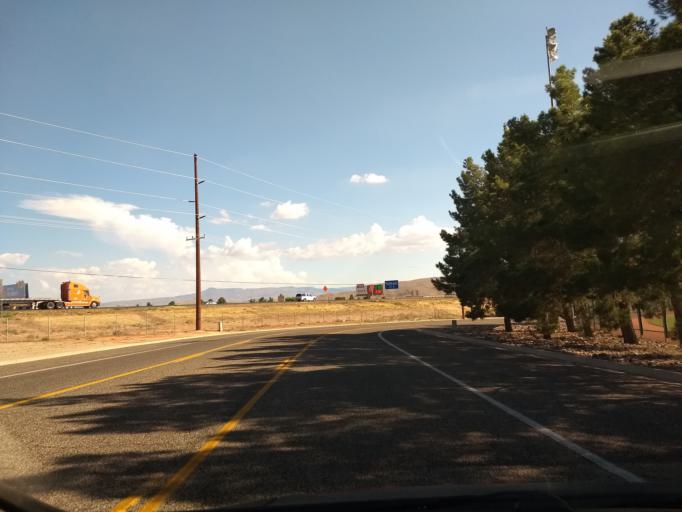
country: US
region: Utah
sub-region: Washington County
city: Saint George
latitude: 37.0988
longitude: -113.5643
